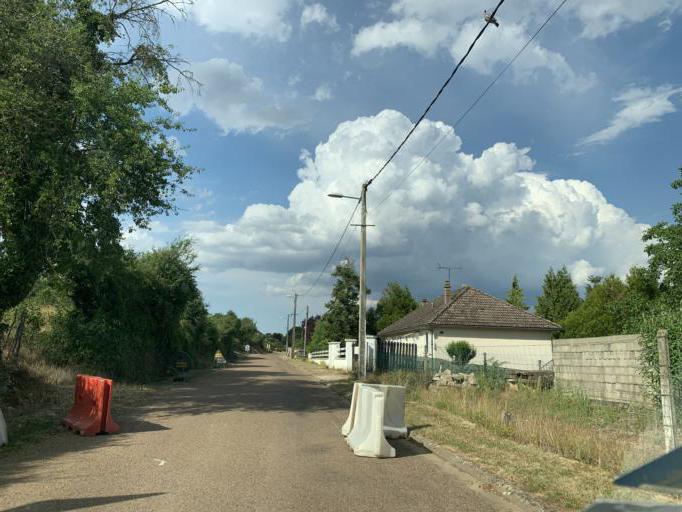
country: FR
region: Bourgogne
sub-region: Departement de la Nievre
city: Varzy
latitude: 47.4485
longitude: 3.4158
